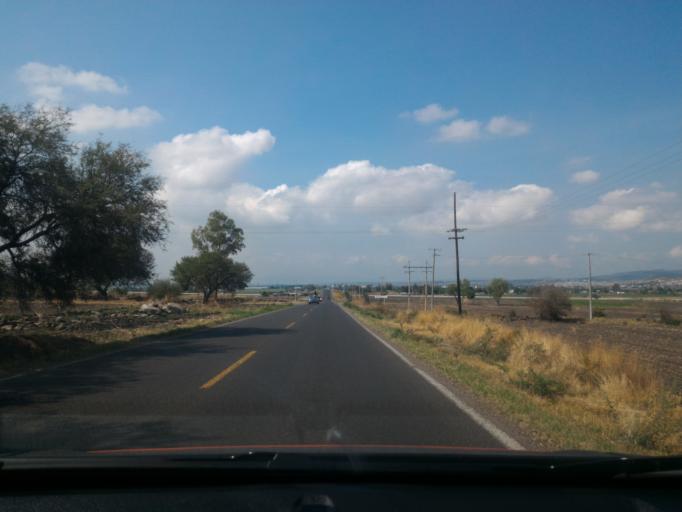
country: MX
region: Guanajuato
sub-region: Penjamo
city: Estacion la Piedad
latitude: 20.4039
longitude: -101.9987
